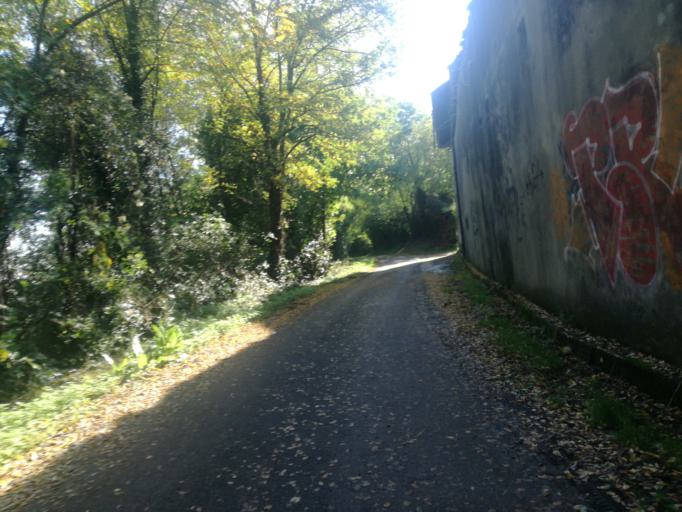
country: IT
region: Lombardy
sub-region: Provincia di Bergamo
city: Bottanuco
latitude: 45.6261
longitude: 9.5026
